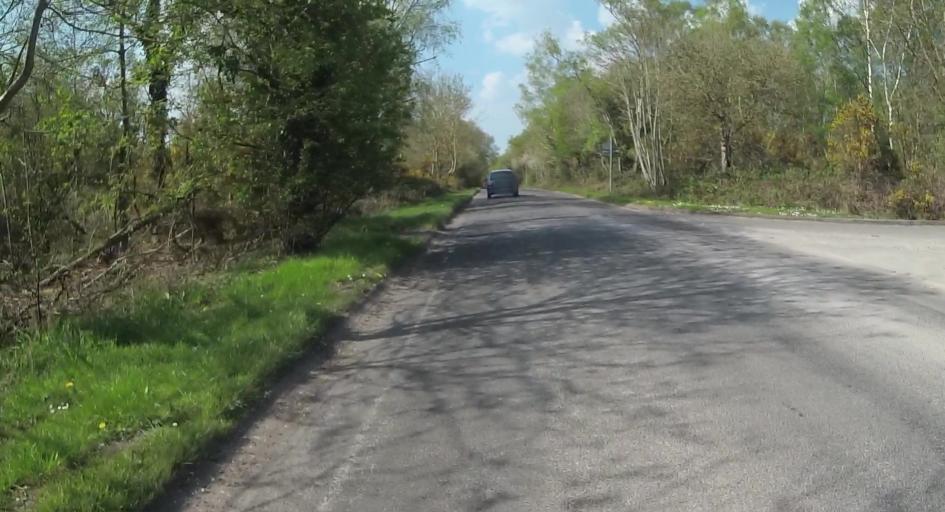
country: GB
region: England
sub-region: Hampshire
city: Tadley
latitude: 51.3550
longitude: -1.1020
